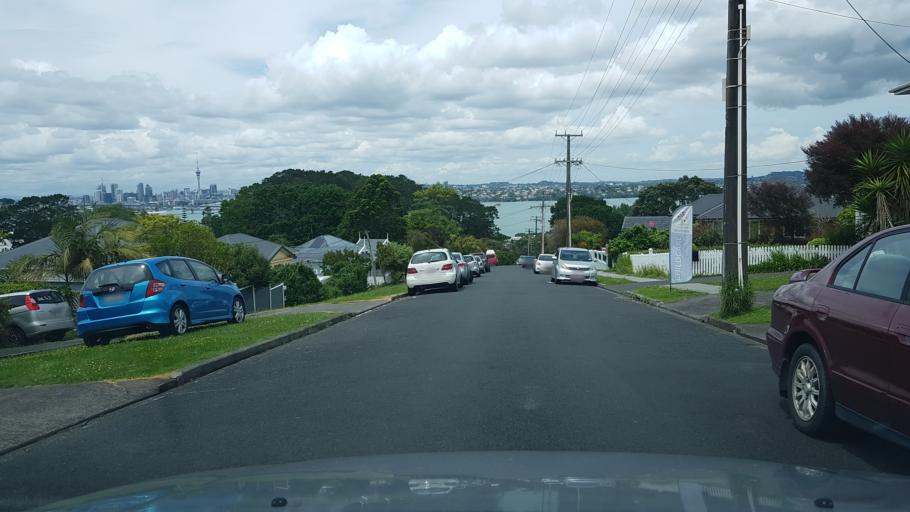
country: NZ
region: Auckland
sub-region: Auckland
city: North Shore
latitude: -36.8140
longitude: 174.7223
